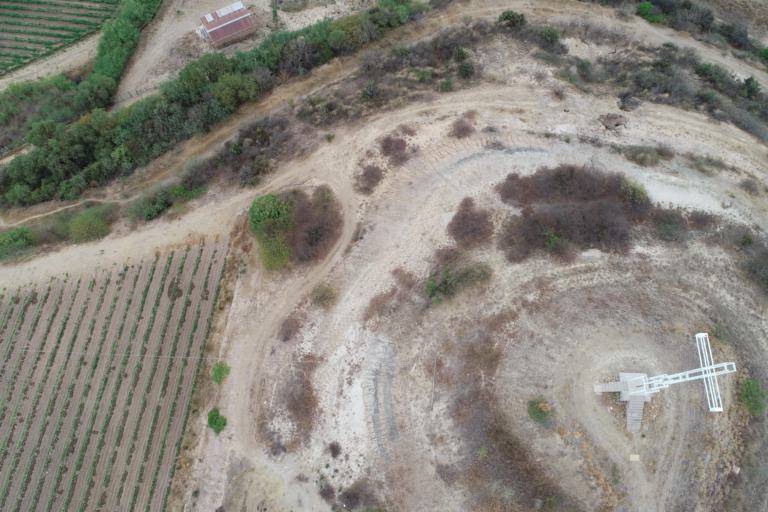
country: BO
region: Tarija
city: Tarija
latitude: -21.5957
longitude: -64.6146
